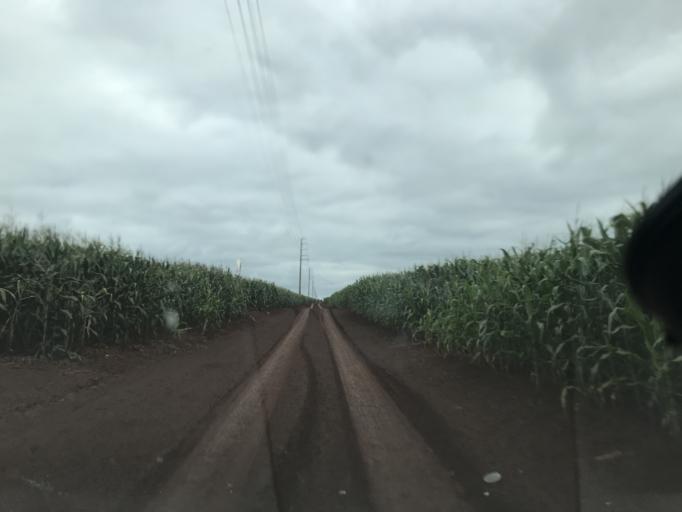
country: BR
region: Parana
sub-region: Palotina
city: Palotina
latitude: -24.3006
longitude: -53.8184
